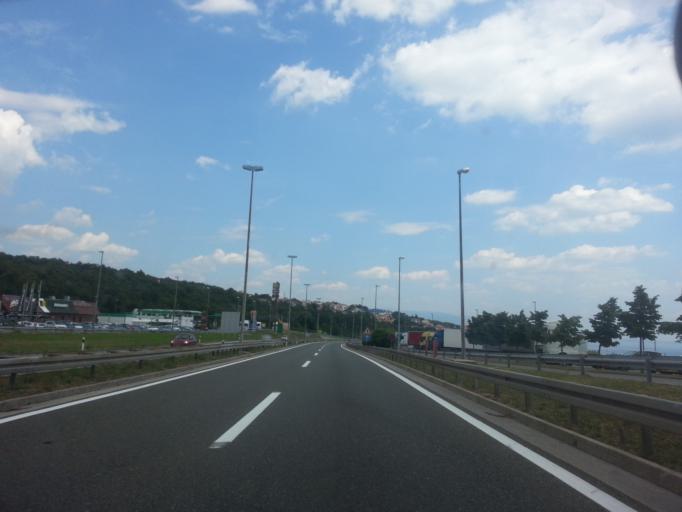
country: HR
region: Primorsko-Goranska
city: Rubesi
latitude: 45.3554
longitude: 14.3508
